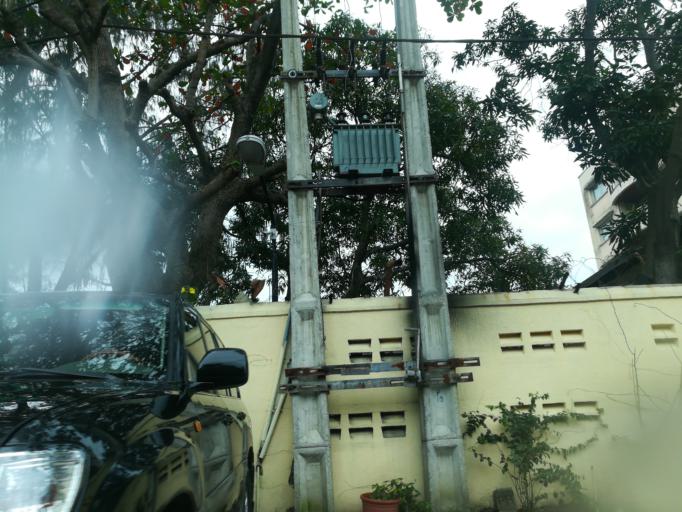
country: NG
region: Lagos
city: Lagos
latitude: 6.4319
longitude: 3.4137
